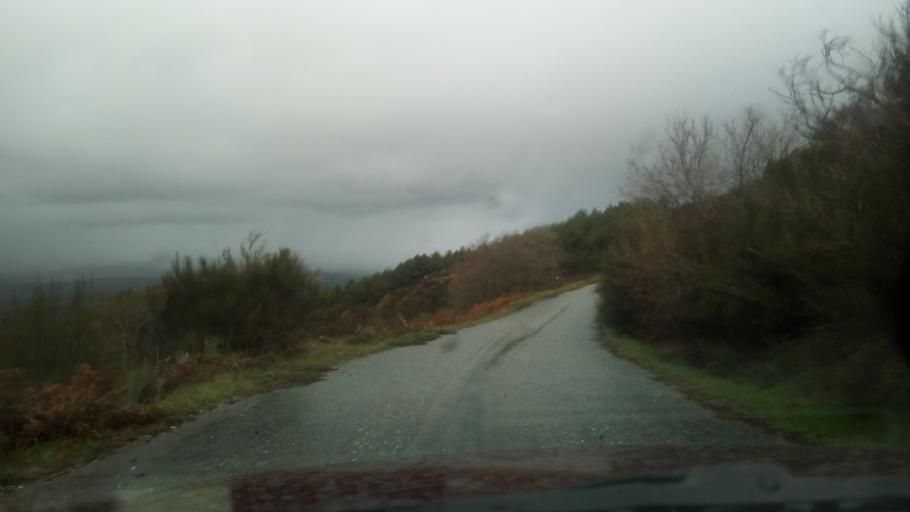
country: PT
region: Guarda
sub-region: Celorico da Beira
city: Celorico da Beira
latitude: 40.5234
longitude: -7.4531
